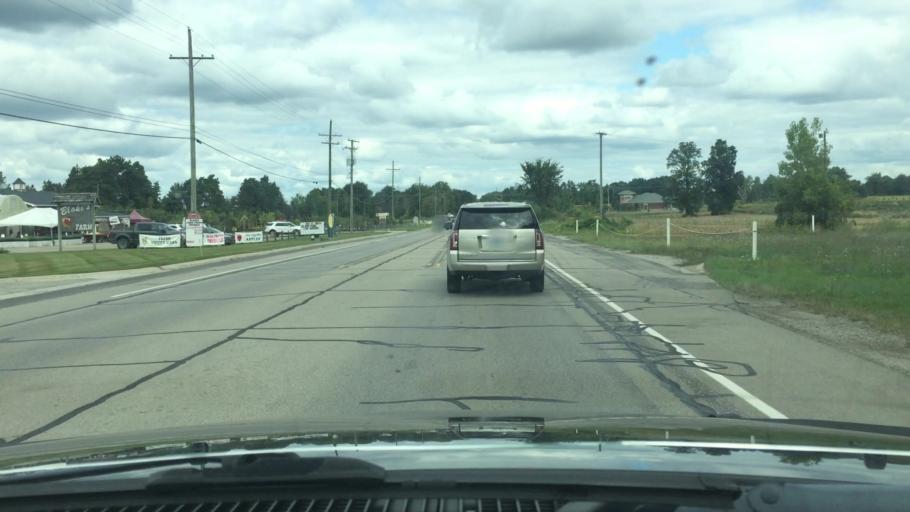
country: US
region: Michigan
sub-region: Lapeer County
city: Almont
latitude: 42.9018
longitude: -83.0440
